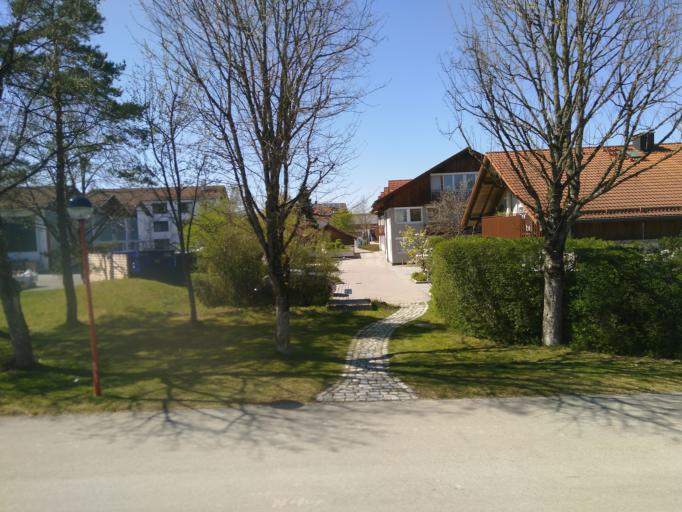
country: DE
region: Bavaria
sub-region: Upper Bavaria
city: Oberhaching
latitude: 48.0304
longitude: 11.5874
